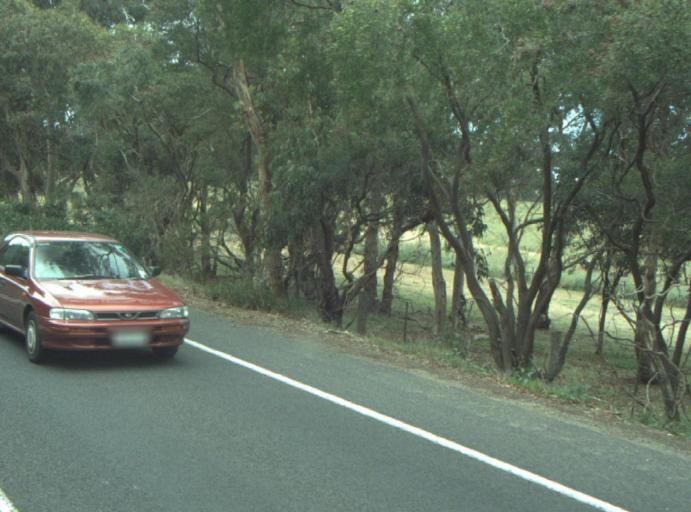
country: AU
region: Victoria
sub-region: Greater Geelong
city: Leopold
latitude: -38.2420
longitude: 144.5031
